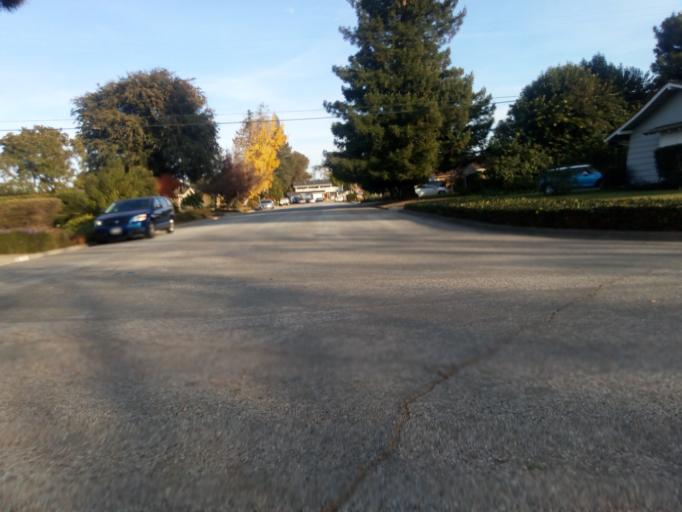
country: US
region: California
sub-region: Santa Clara County
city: Sunnyvale
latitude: 37.3590
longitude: -122.0653
